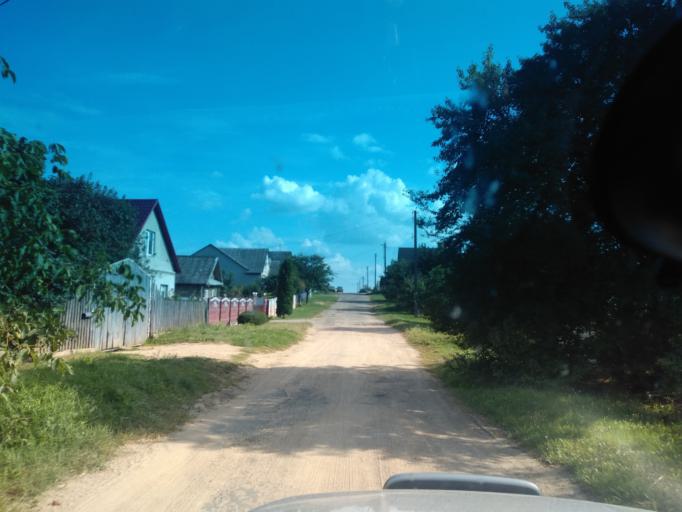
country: BY
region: Minsk
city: Kapyl'
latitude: 53.1532
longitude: 27.0770
